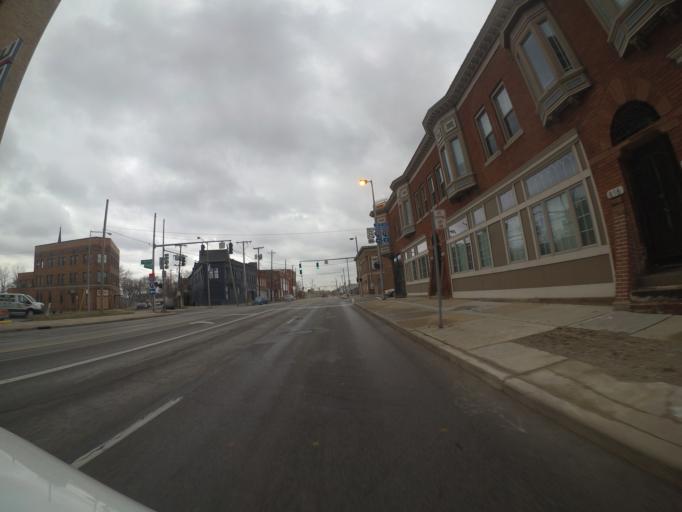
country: US
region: Ohio
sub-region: Lucas County
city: Toledo
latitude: 41.6496
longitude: -83.5427
